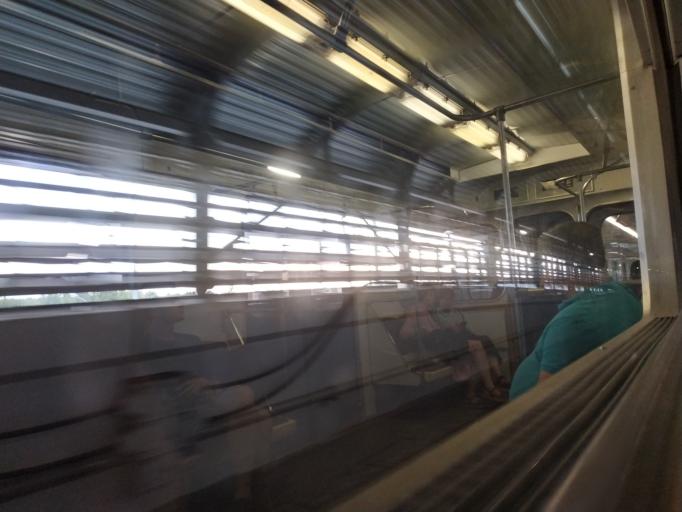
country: RU
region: Moscow
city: Solntsevo
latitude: 55.5975
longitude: 37.4142
